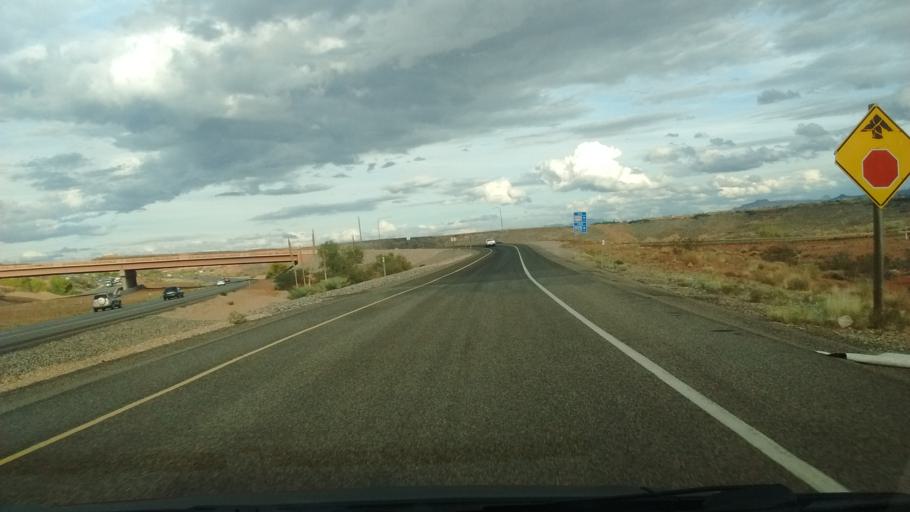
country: US
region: Utah
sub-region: Washington County
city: Washington
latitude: 37.1456
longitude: -113.4896
